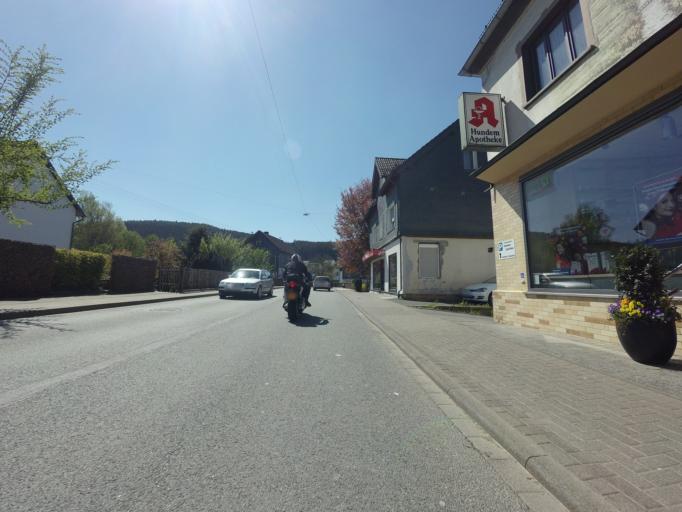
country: DE
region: North Rhine-Westphalia
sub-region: Regierungsbezirk Arnsberg
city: Kirchhundem
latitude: 51.0864
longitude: 8.1210
